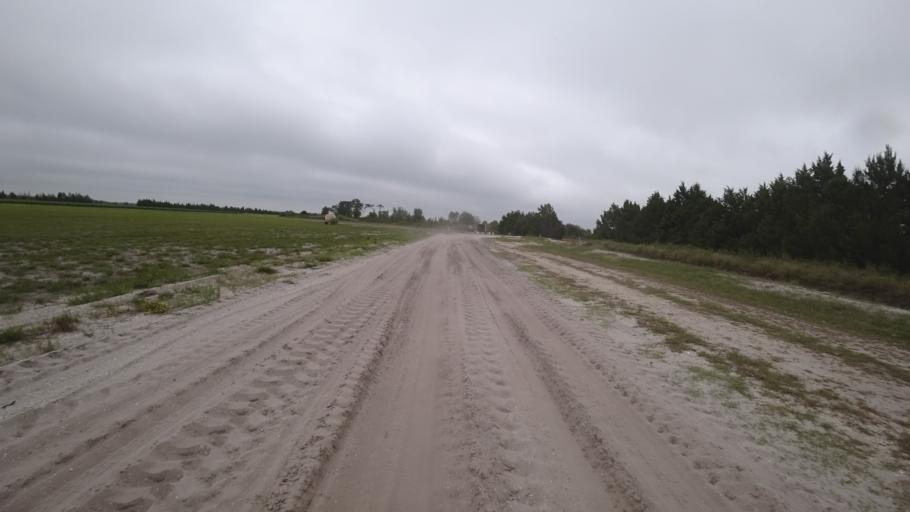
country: US
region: Florida
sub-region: Sarasota County
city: Warm Mineral Springs
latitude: 27.3004
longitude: -82.1471
